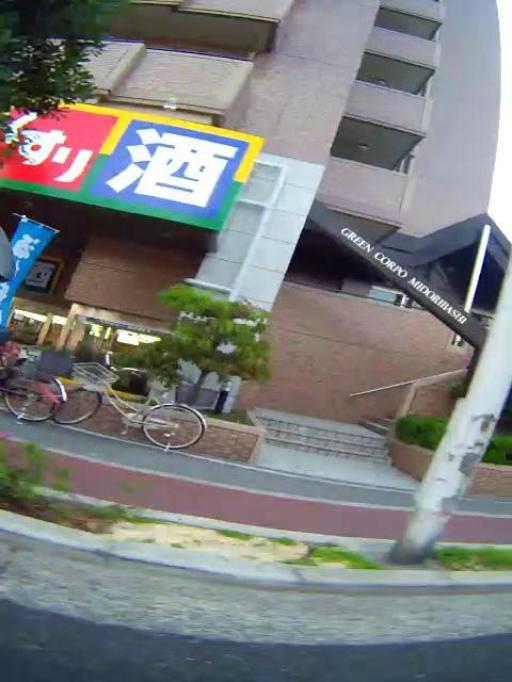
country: JP
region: Osaka
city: Osaka-shi
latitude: 34.6852
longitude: 135.5451
